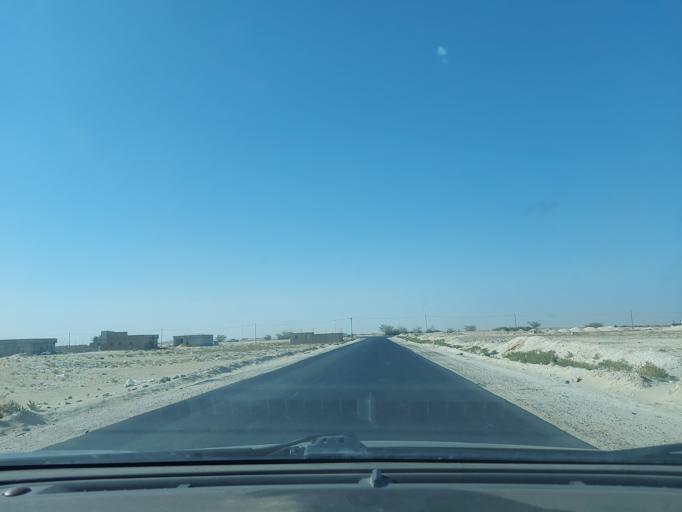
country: MR
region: Nouakchott
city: Nouakchott
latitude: 17.9943
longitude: -15.9882
